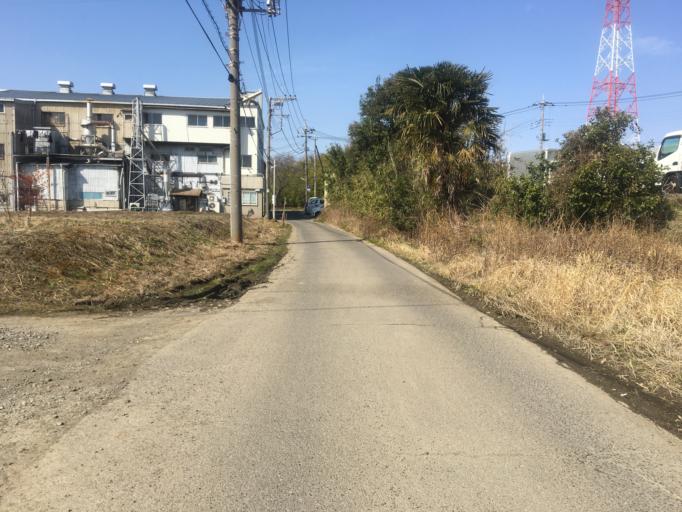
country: JP
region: Saitama
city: Shiki
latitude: 35.8300
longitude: 139.6053
